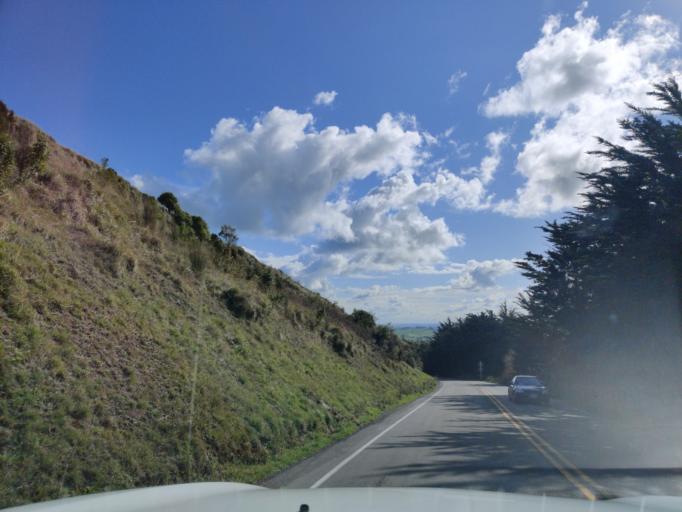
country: NZ
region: Manawatu-Wanganui
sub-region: Palmerston North City
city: Palmerston North
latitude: -40.2884
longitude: 175.7943
